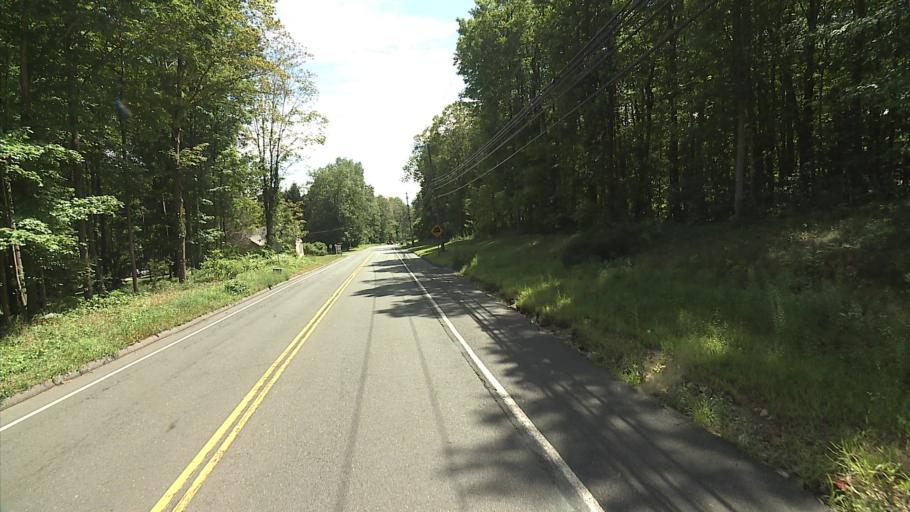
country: US
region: Connecticut
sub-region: Tolland County
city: Tolland
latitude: 41.8513
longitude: -72.3310
